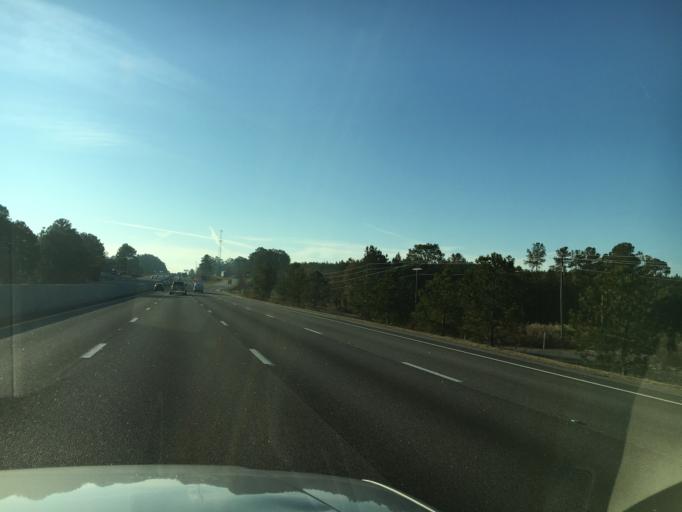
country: US
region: South Carolina
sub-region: Lexington County
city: Gaston
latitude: 33.8438
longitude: -81.0247
